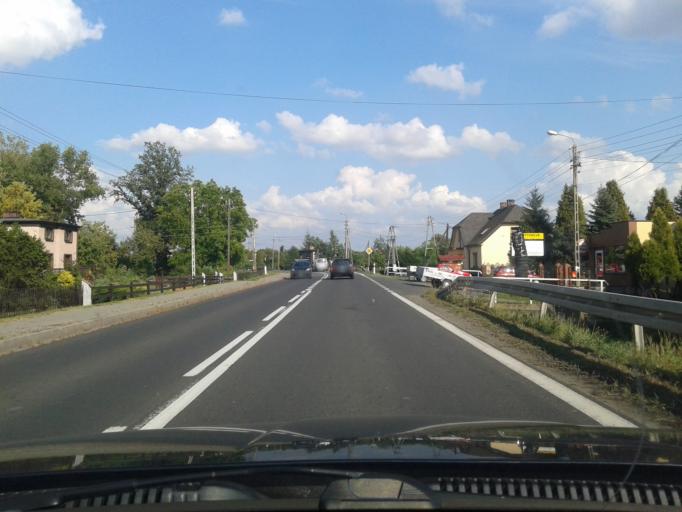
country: PL
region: Silesian Voivodeship
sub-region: Powiat wodzislawski
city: Olza
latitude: 49.9549
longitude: 18.3521
